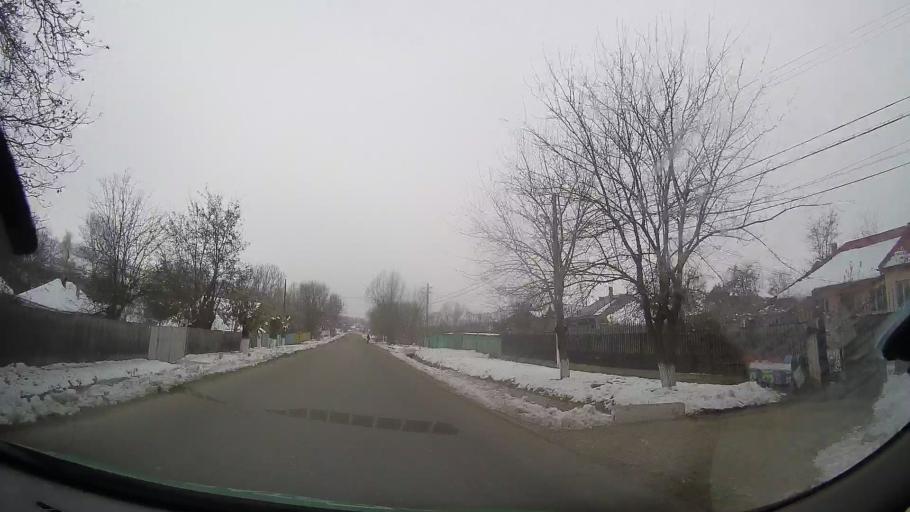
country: RO
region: Bacau
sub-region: Comuna Glavanesti
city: Frumuselu
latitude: 46.2954
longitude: 27.3005
